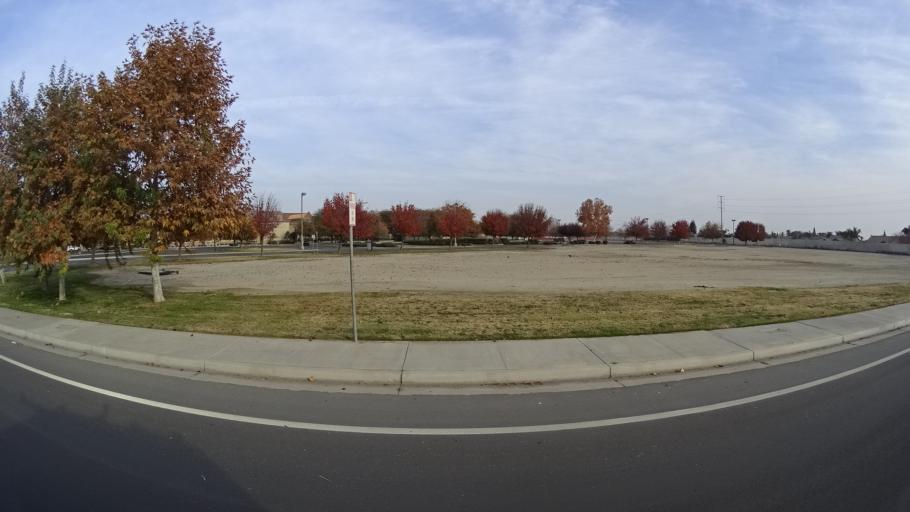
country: US
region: California
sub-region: Kern County
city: Greenacres
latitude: 35.3120
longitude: -119.1280
